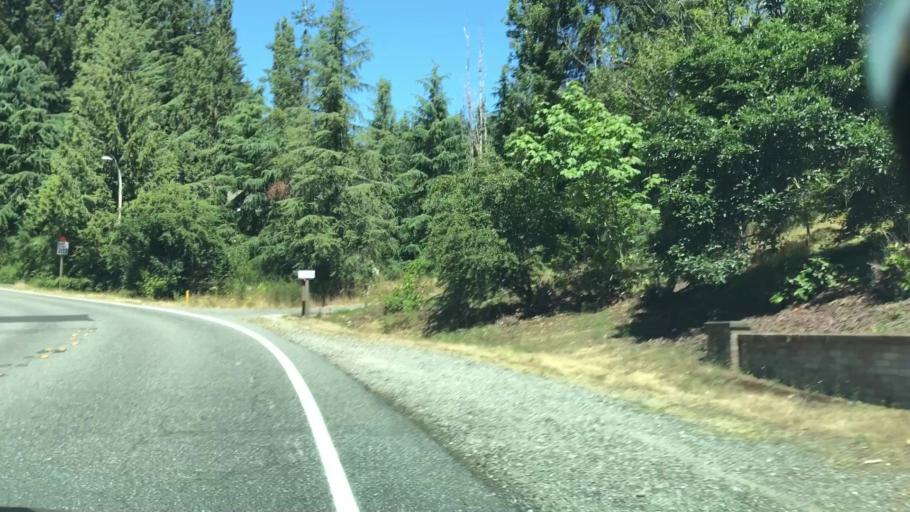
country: US
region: Washington
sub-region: King County
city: Cottage Lake
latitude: 47.7549
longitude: -122.0776
